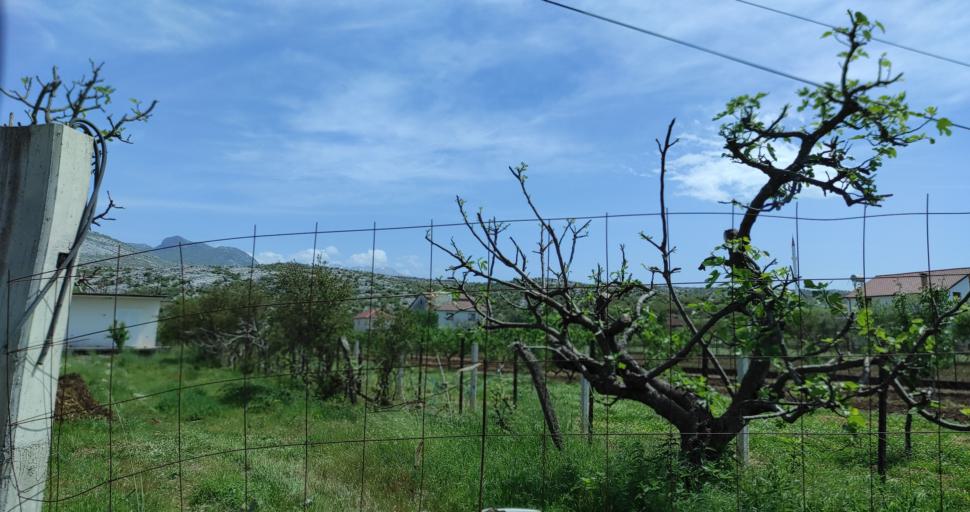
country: AL
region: Shkoder
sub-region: Rrethi i Malesia e Madhe
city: Gruemire
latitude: 42.1317
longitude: 19.5503
